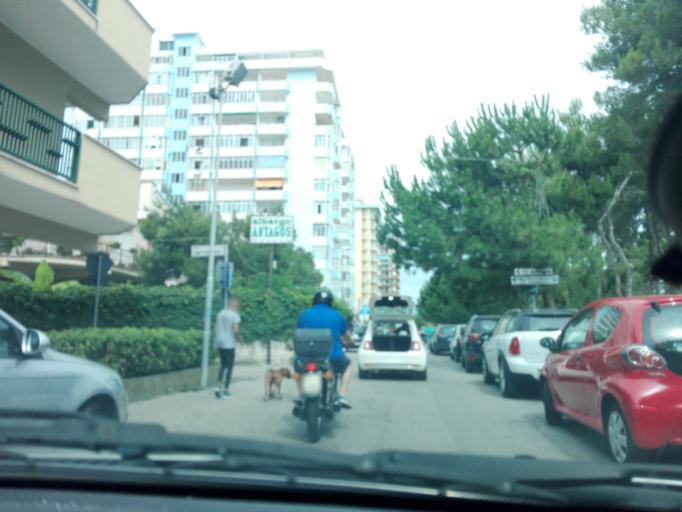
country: IT
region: Abruzzo
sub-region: Provincia di Pescara
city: Villa Raspa
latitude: 42.4961
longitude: 14.1815
